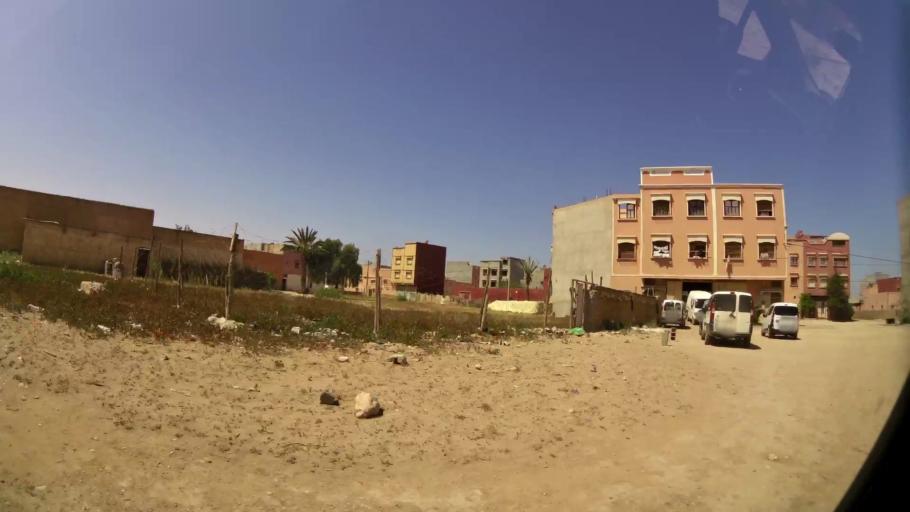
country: MA
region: Souss-Massa-Draa
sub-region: Inezgane-Ait Mellou
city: Inezgane
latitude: 30.3156
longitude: -9.5037
